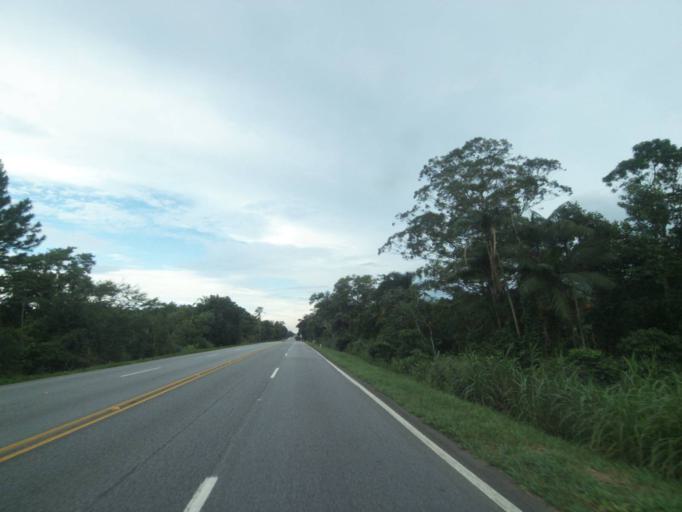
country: BR
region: Parana
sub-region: Pontal Do Parana
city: Pontal do Parana
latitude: -25.6382
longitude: -48.5925
